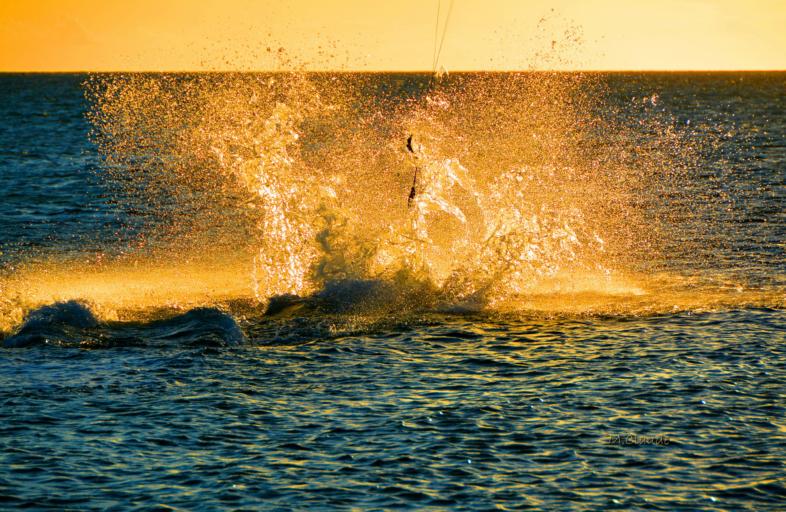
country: NC
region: South Province
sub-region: Noumea
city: Noumea
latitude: -22.3119
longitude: 166.4483
